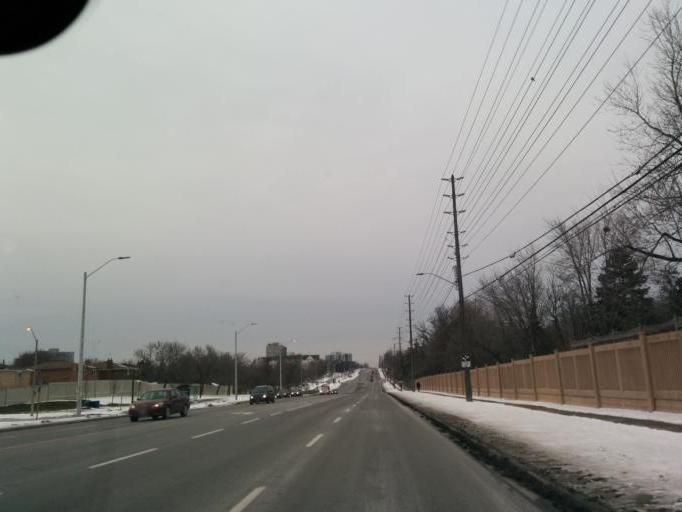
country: CA
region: Ontario
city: Etobicoke
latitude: 43.6160
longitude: -79.6096
